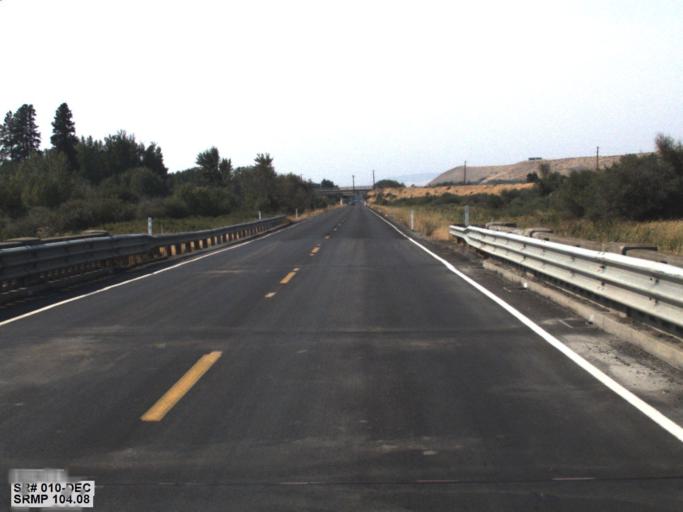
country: US
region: Washington
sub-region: Kittitas County
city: Ellensburg
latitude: 47.0383
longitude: -120.6163
